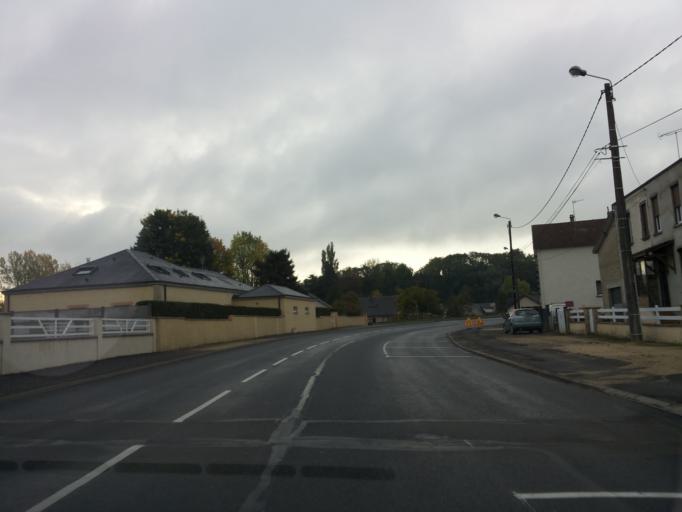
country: FR
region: Champagne-Ardenne
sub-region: Departement des Ardennes
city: Flize
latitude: 49.7026
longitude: 4.7741
